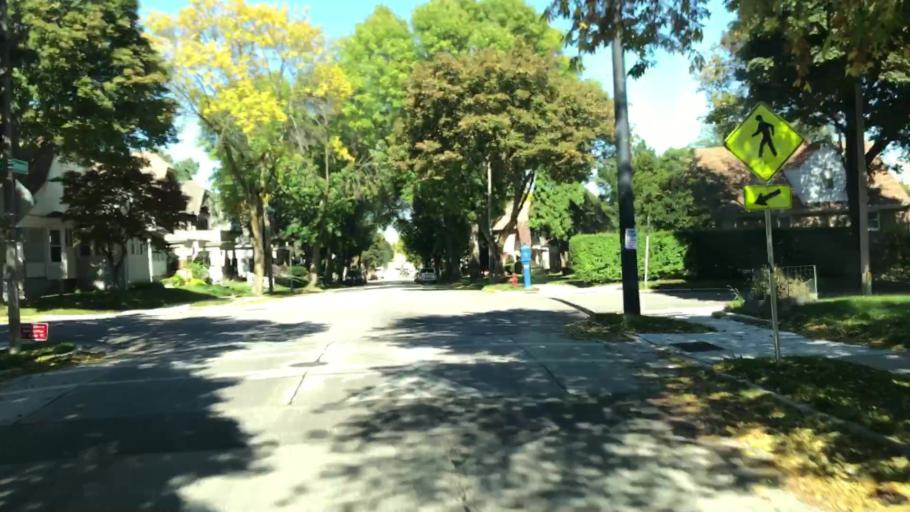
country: US
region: Wisconsin
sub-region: Milwaukee County
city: Saint Francis
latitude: 42.9922
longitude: -87.8943
